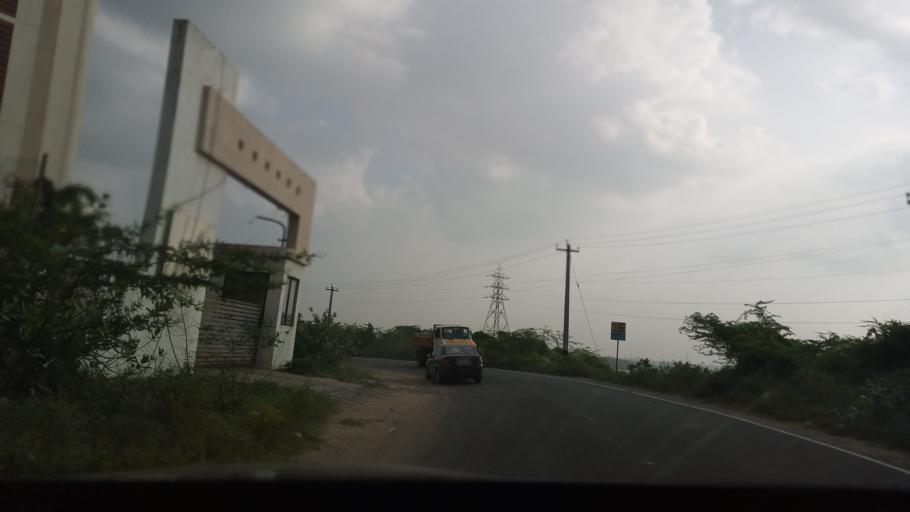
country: IN
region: Tamil Nadu
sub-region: Kancheepuram
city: Vengavasal
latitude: 12.7823
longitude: 80.2303
